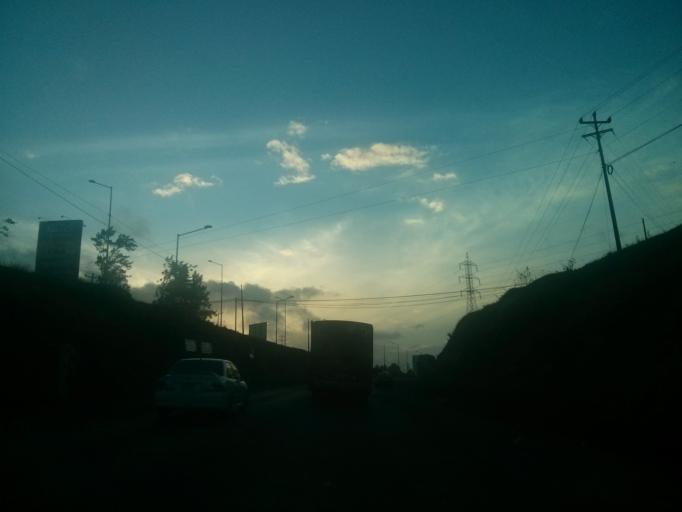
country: CR
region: Cartago
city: Cartago
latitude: 9.8913
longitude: -83.9395
